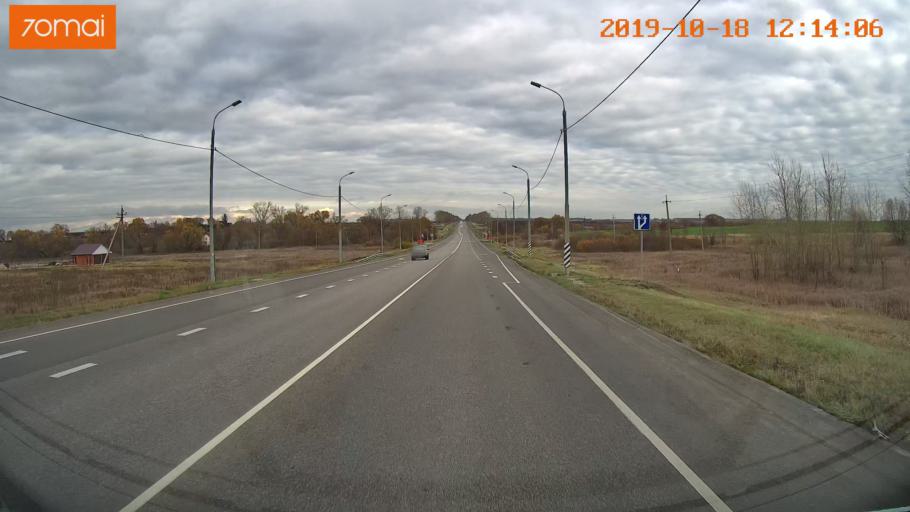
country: RU
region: Rjazan
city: Zakharovo
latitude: 54.4264
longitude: 39.3776
